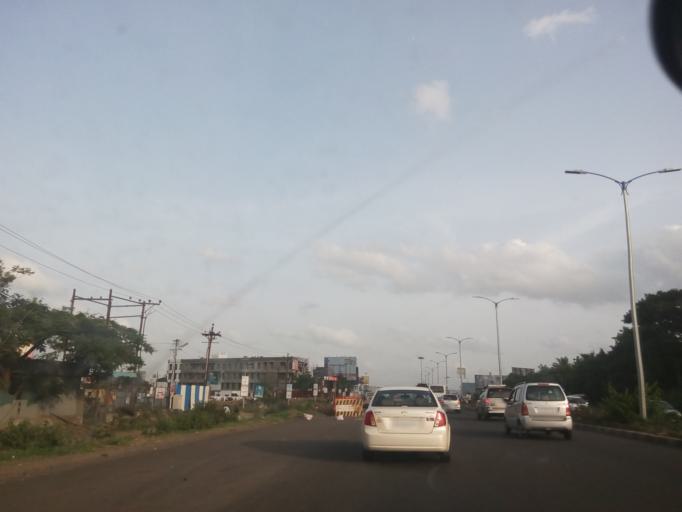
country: IN
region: Maharashtra
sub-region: Pune Division
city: Pimpri
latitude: 18.6106
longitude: 73.7503
